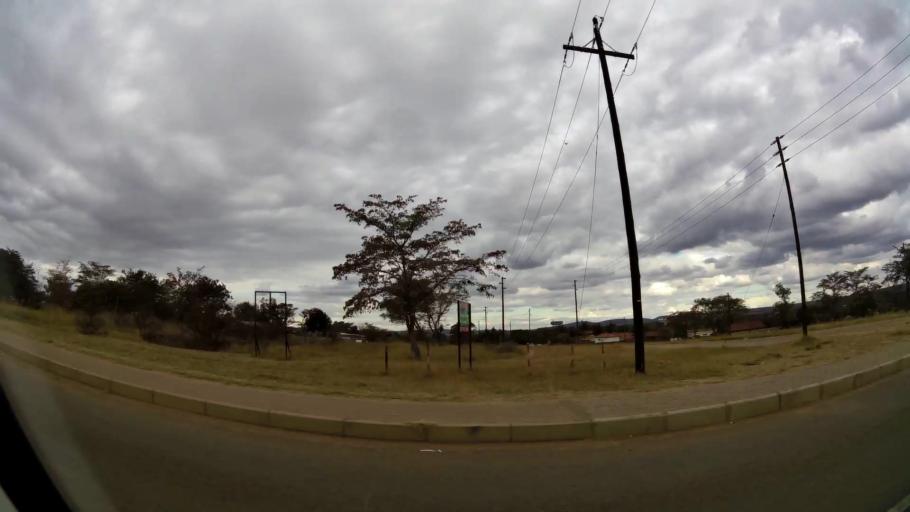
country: ZA
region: Limpopo
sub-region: Waterberg District Municipality
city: Modimolle
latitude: -24.6977
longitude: 28.4193
